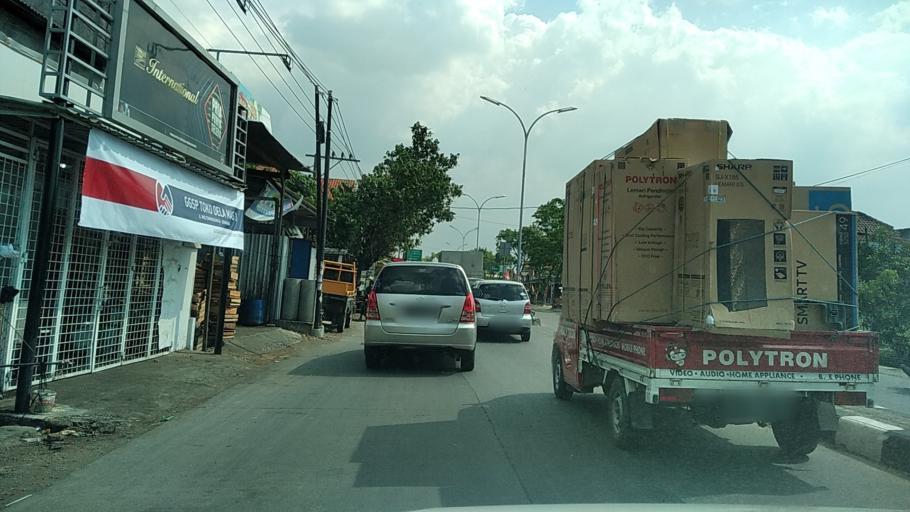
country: ID
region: Central Java
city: Semarang
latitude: -6.9575
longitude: 110.4798
